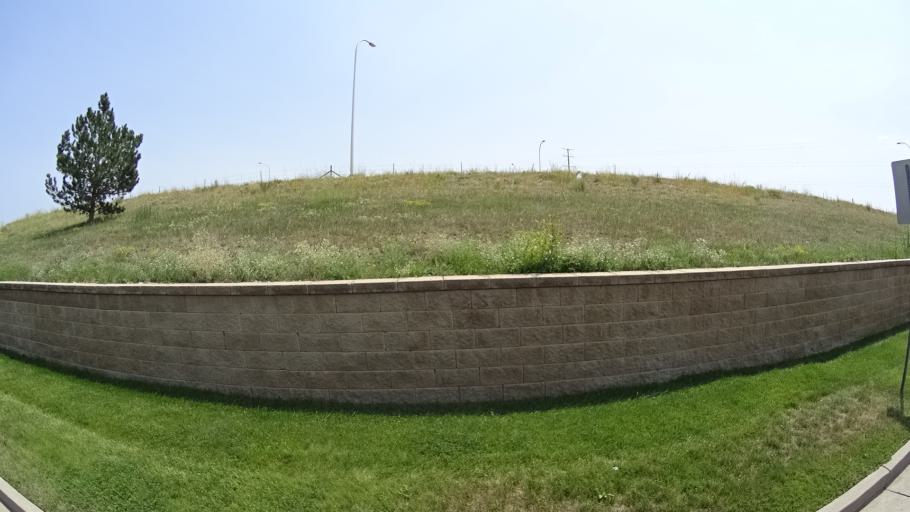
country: US
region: Colorado
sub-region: El Paso County
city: Black Forest
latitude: 38.9419
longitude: -104.7227
